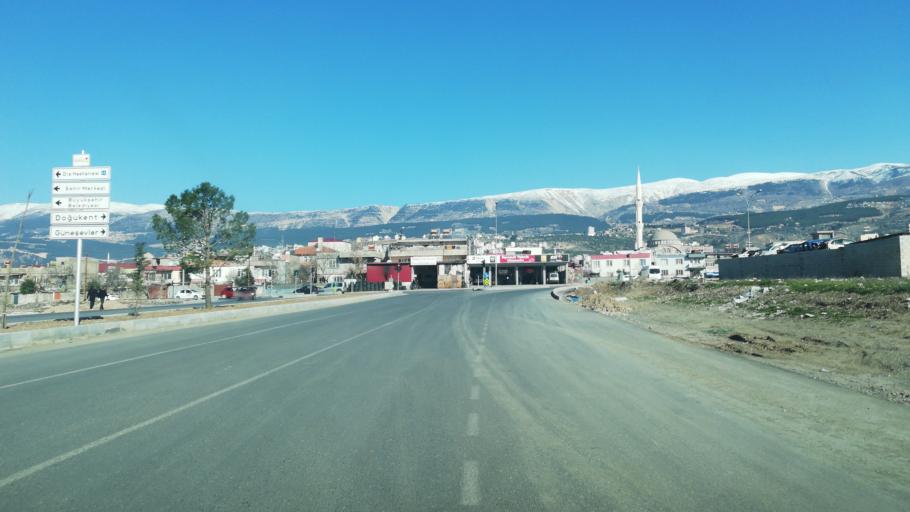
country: TR
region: Kahramanmaras
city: Kahramanmaras
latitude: 37.5692
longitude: 36.9634
